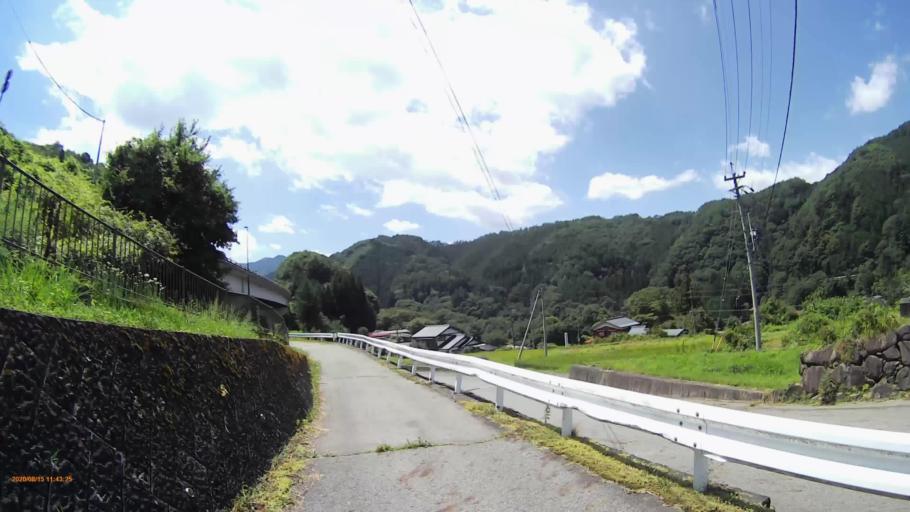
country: JP
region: Nagano
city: Ina
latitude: 35.8324
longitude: 137.6827
